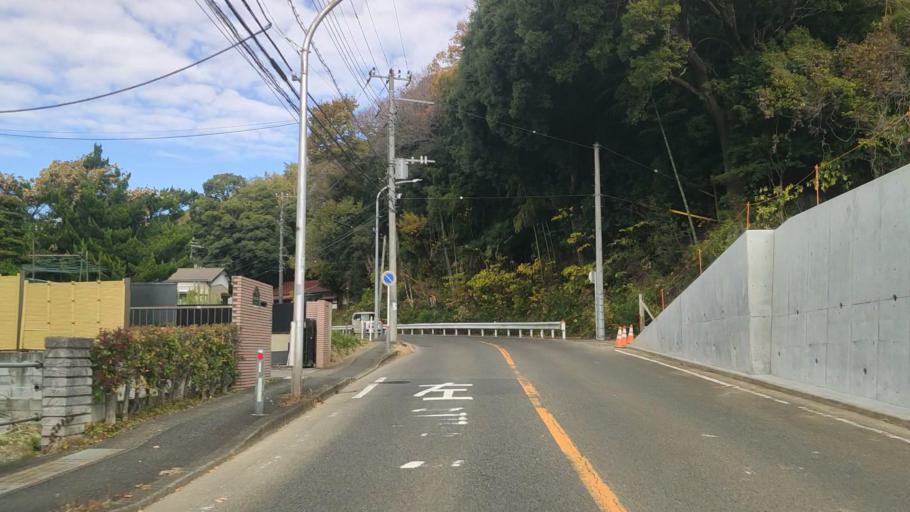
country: JP
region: Kanagawa
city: Yokohama
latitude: 35.4366
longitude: 139.5449
